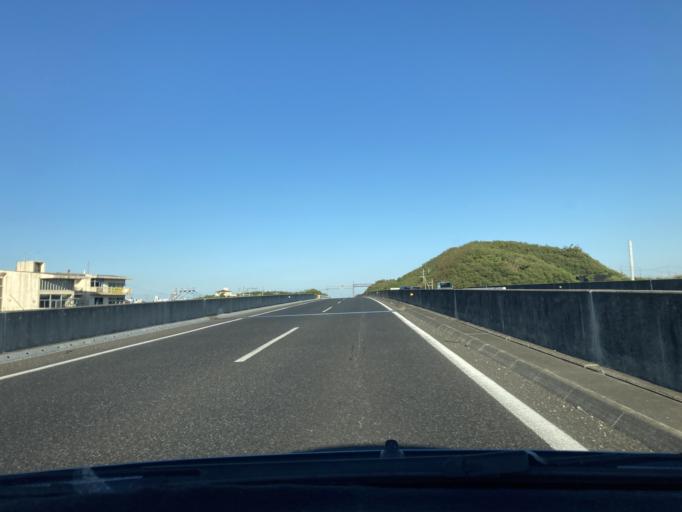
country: JP
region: Okinawa
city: Tomigusuku
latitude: 26.1745
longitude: 127.7041
